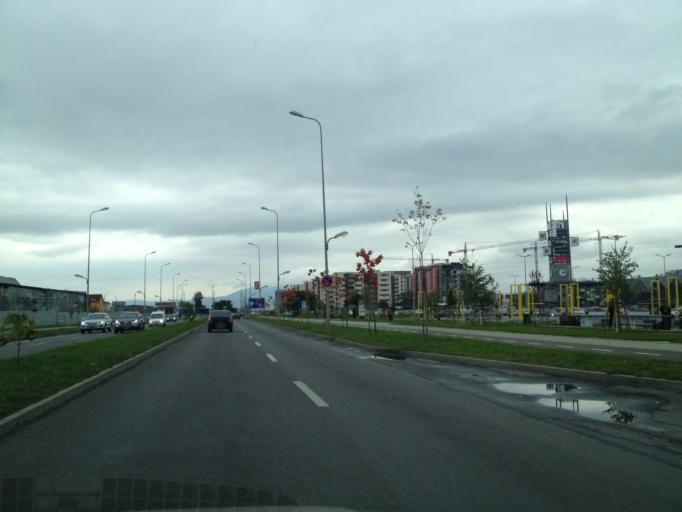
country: RO
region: Brasov
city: Brasov
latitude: 45.6709
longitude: 25.6152
